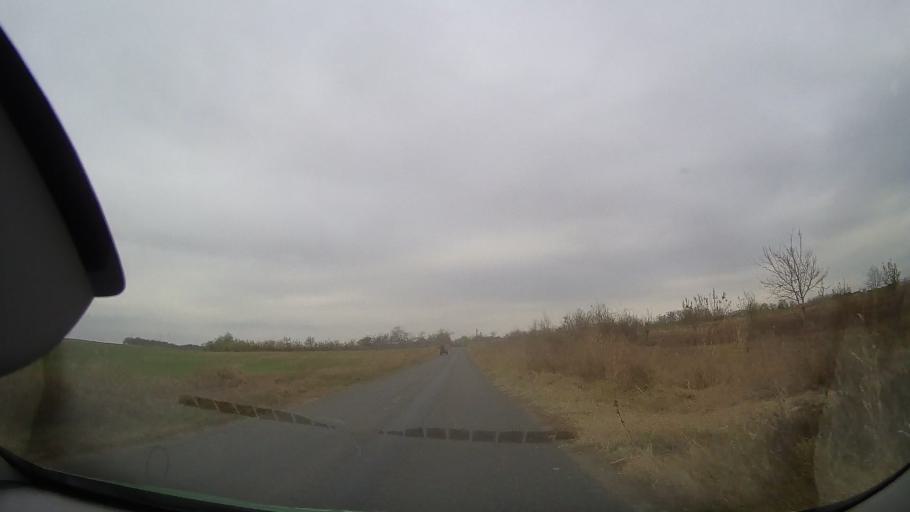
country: RO
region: Buzau
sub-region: Comuna Largu
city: Largu
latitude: 44.9694
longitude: 27.1844
